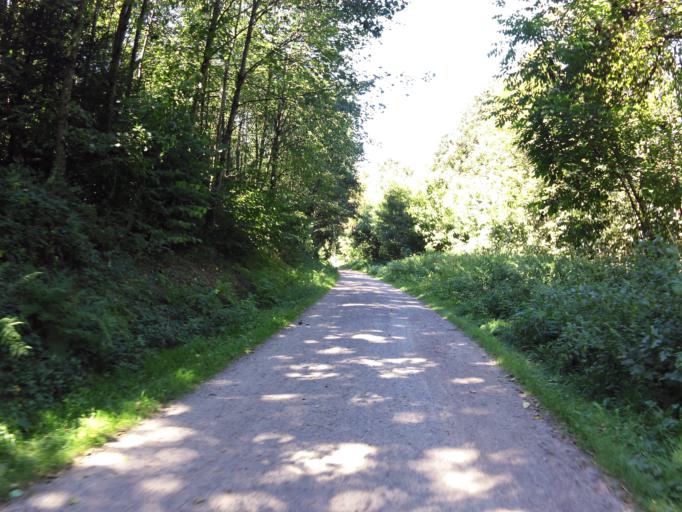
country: DE
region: Baden-Wuerttemberg
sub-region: Freiburg Region
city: Hohberg
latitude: 48.3378
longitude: 7.8984
